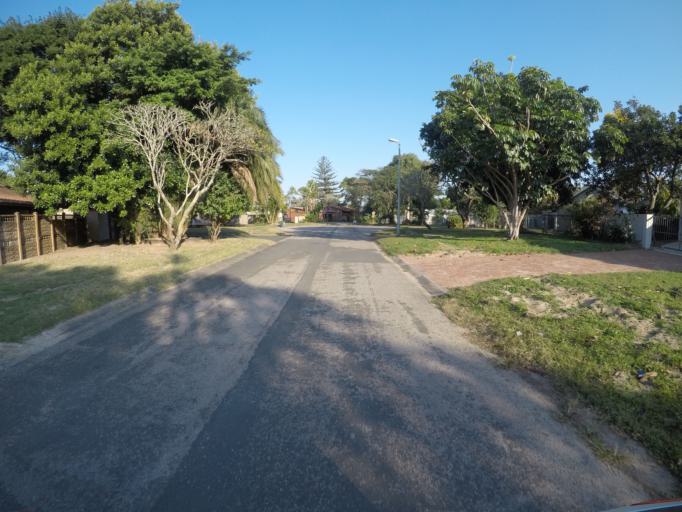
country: ZA
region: KwaZulu-Natal
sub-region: uThungulu District Municipality
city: Richards Bay
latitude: -28.7764
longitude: 32.1015
